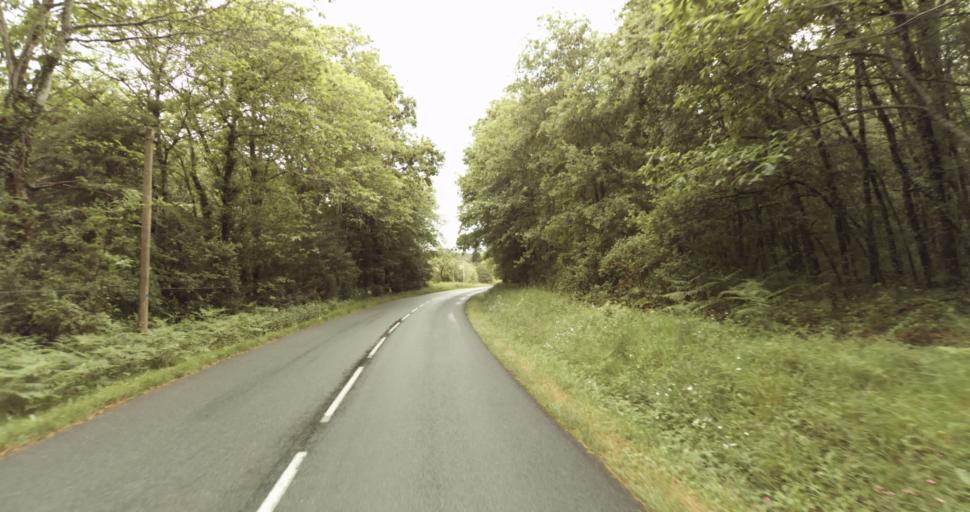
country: FR
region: Aquitaine
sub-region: Departement de la Dordogne
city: Belves
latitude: 44.7137
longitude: 0.9343
